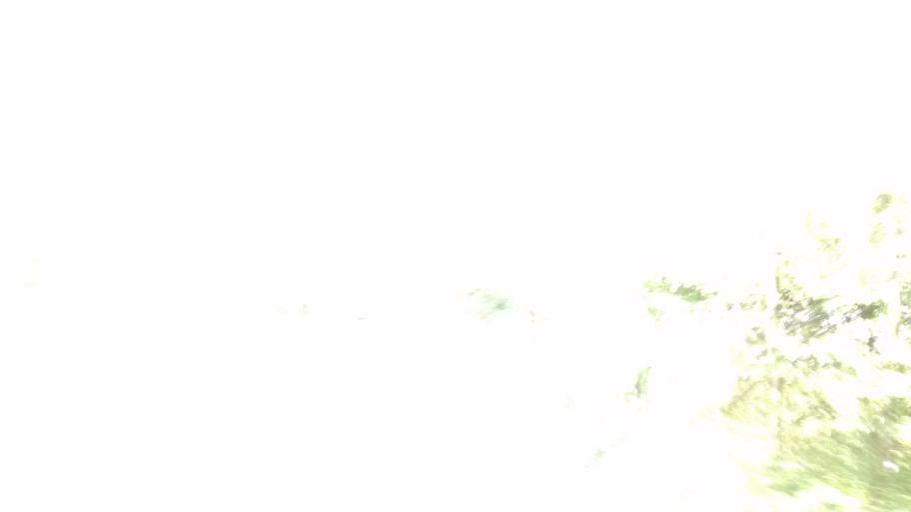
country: FR
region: Brittany
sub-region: Departement du Morbihan
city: Malestroit
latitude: 47.7847
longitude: -2.3896
